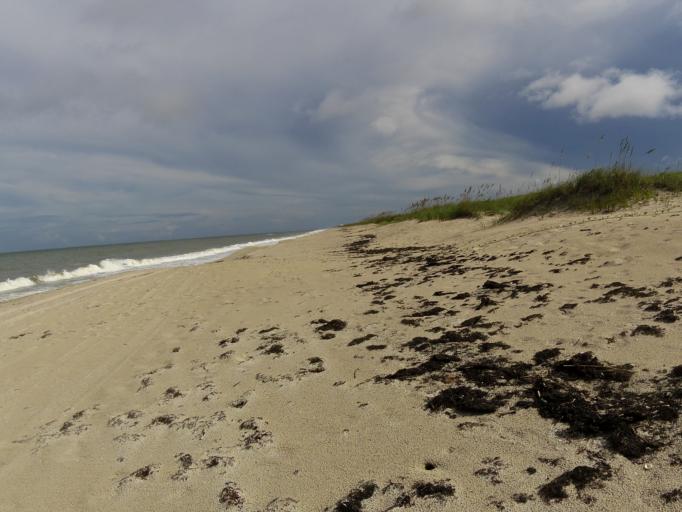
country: US
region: Florida
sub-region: Indian River County
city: Sebastian
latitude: 27.8502
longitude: -80.4421
